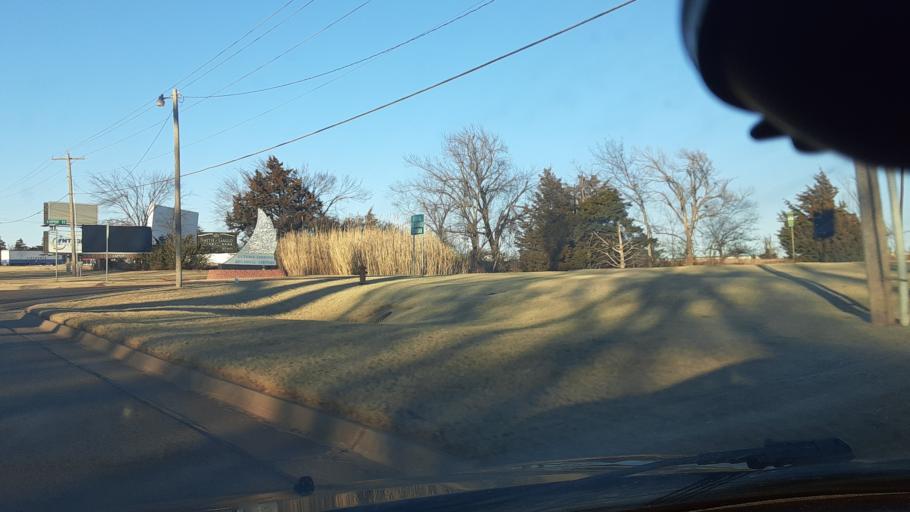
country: US
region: Oklahoma
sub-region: Logan County
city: Guthrie
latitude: 35.8520
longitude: -97.4254
